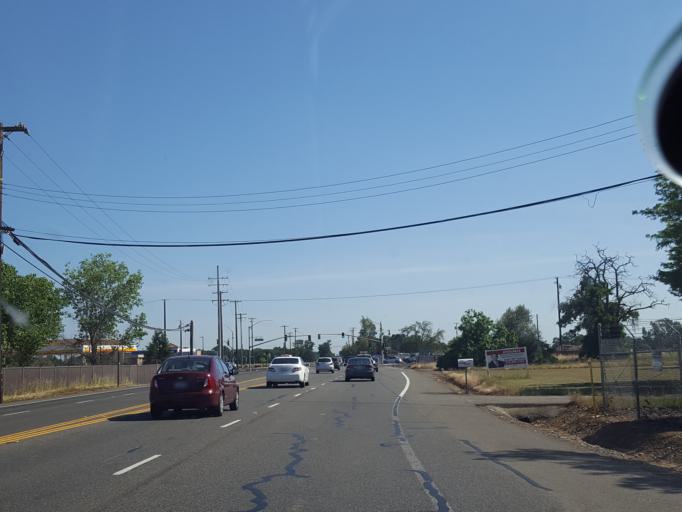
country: US
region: California
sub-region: Sacramento County
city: Rosemont
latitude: 38.5309
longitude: -121.3350
